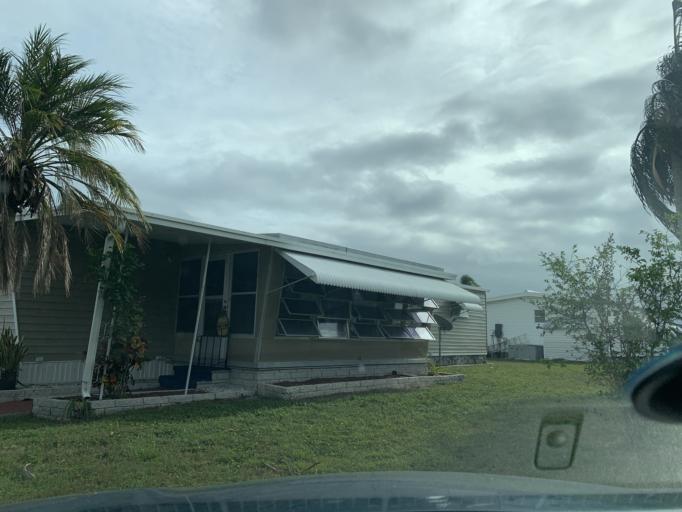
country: US
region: Florida
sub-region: Pinellas County
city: Largo
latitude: 27.8896
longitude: -82.7787
